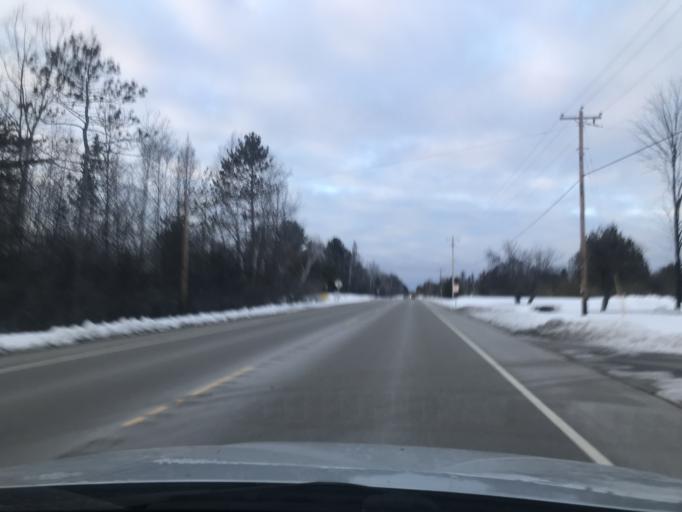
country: US
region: Wisconsin
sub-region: Marinette County
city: Marinette
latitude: 45.1203
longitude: -87.6825
